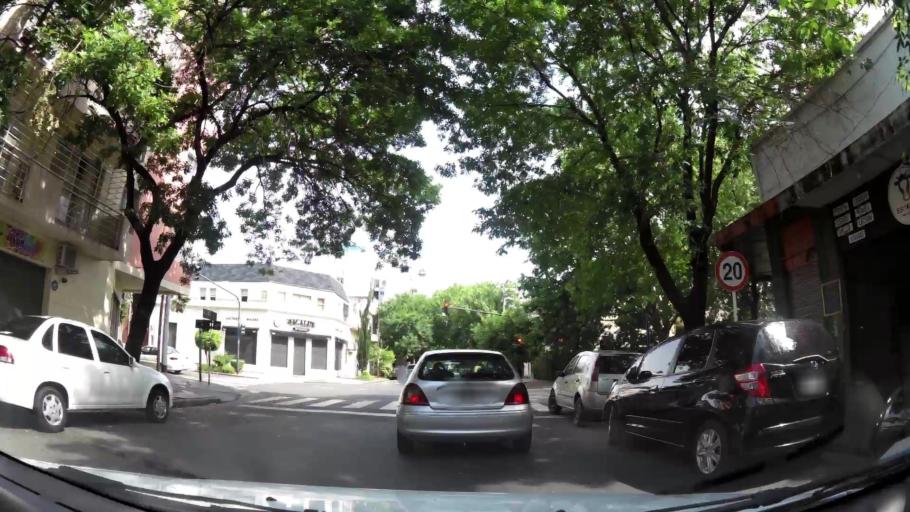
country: AR
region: Buenos Aires
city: San Justo
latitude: -34.6443
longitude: -58.5205
